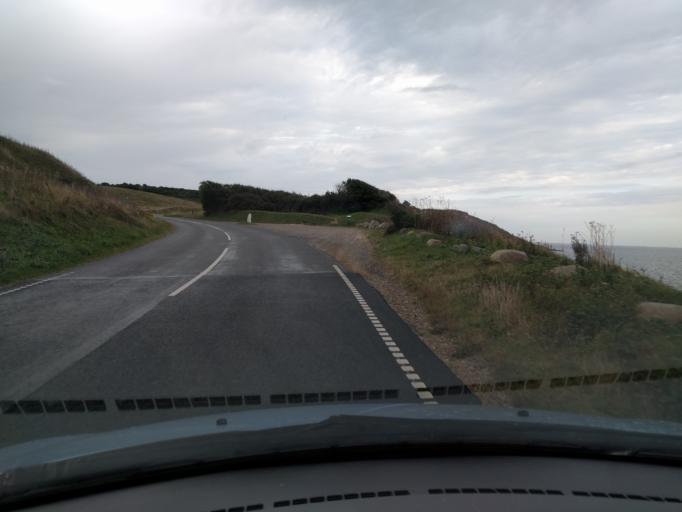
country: DK
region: South Denmark
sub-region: Assens Kommune
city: Assens
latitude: 55.1751
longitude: 9.9855
